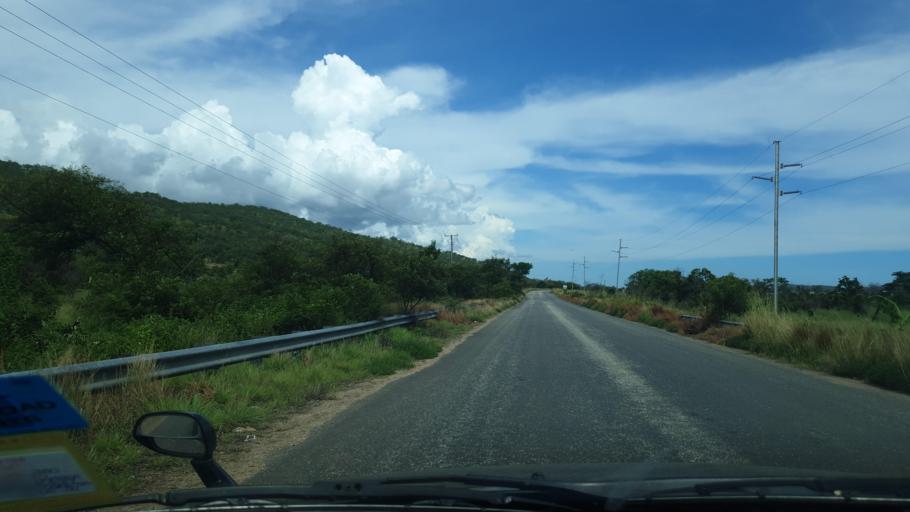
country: PG
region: National Capital
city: Port Moresby
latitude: -9.4074
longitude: 147.0686
